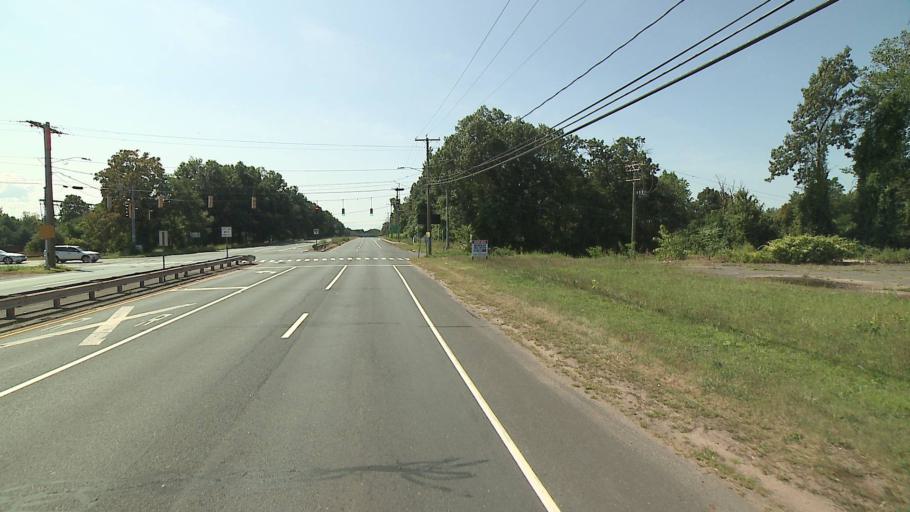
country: US
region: Connecticut
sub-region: Hartford County
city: South Windsor
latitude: 41.8119
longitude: -72.6123
